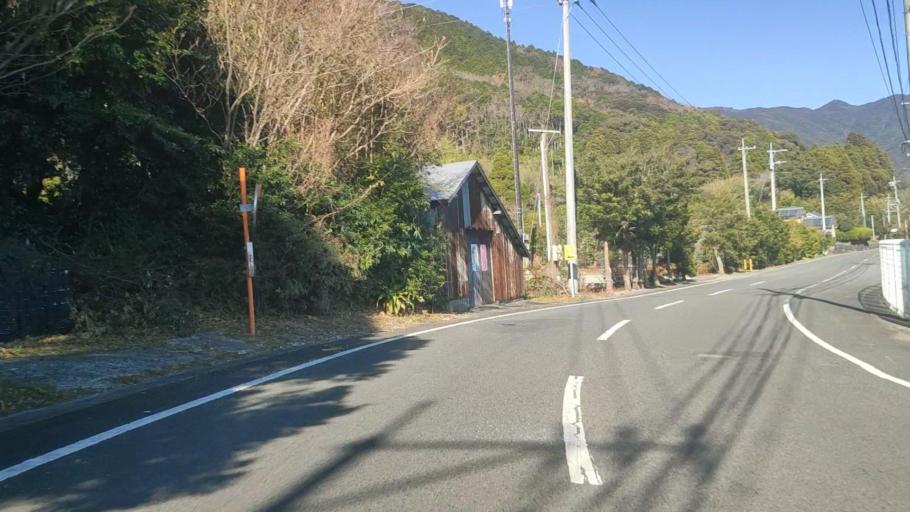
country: JP
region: Oita
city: Saiki
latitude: 32.8009
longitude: 131.8882
